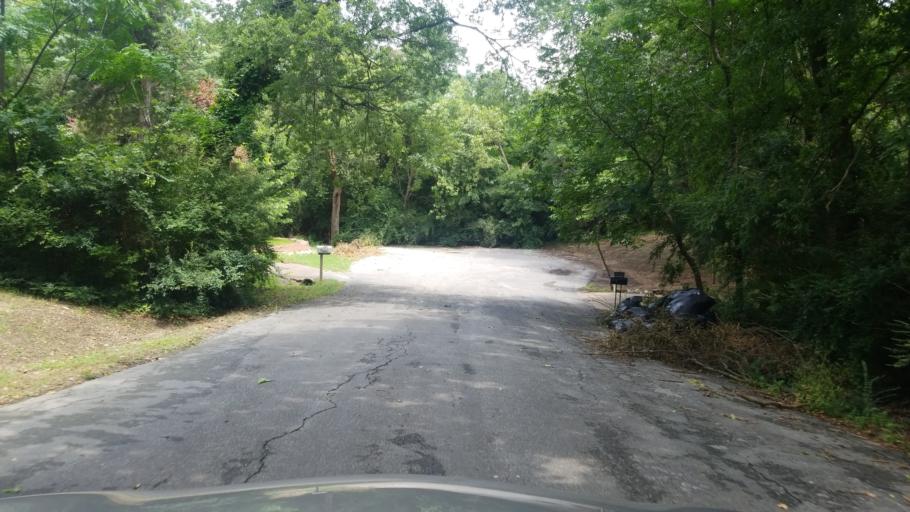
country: US
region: Texas
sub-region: Dallas County
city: Duncanville
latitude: 32.6833
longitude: -96.9153
